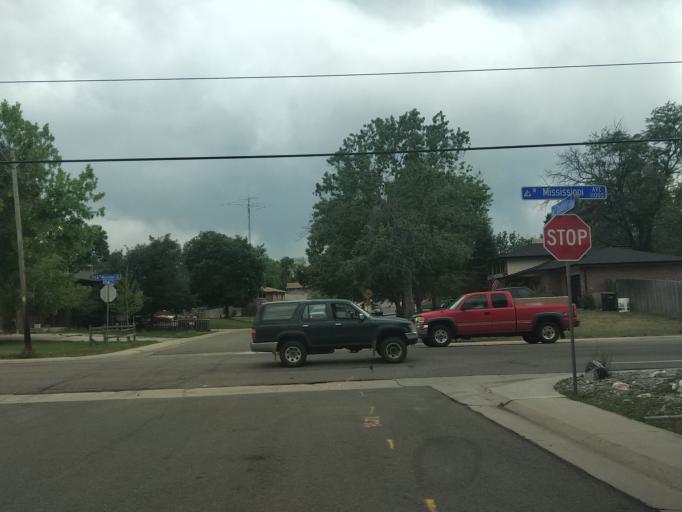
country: US
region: Colorado
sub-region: Jefferson County
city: Lakewood
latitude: 39.6968
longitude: -105.0947
